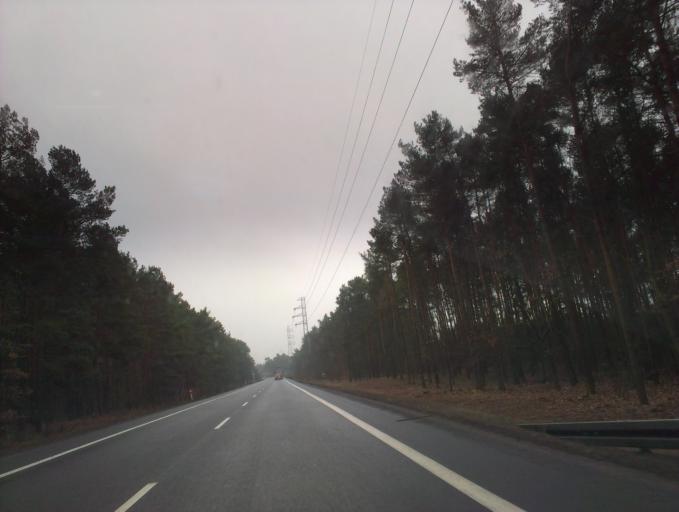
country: PL
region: Greater Poland Voivodeship
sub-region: Powiat pilski
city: Pila
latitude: 53.1556
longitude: 16.7878
